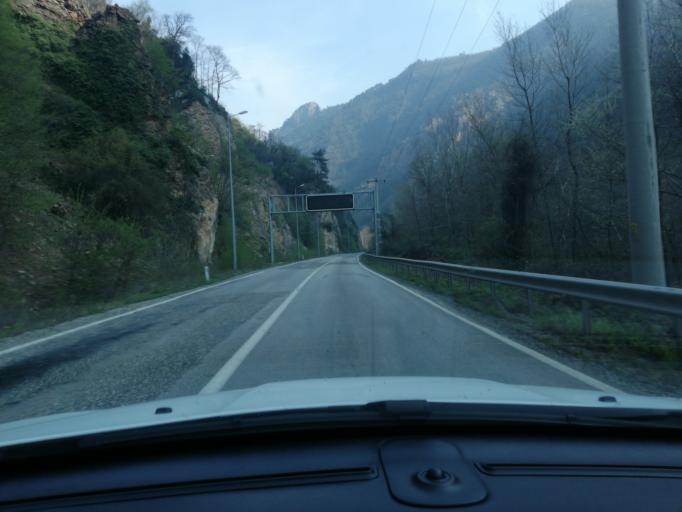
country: TR
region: Karabuk
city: Yenice
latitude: 41.1765
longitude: 32.4468
